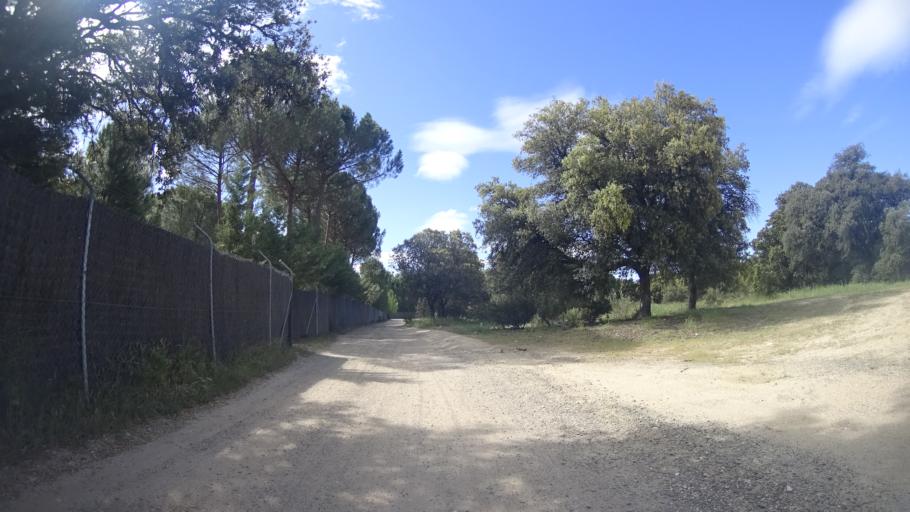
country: ES
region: Madrid
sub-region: Provincia de Madrid
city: Brunete
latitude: 40.4202
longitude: -3.9495
